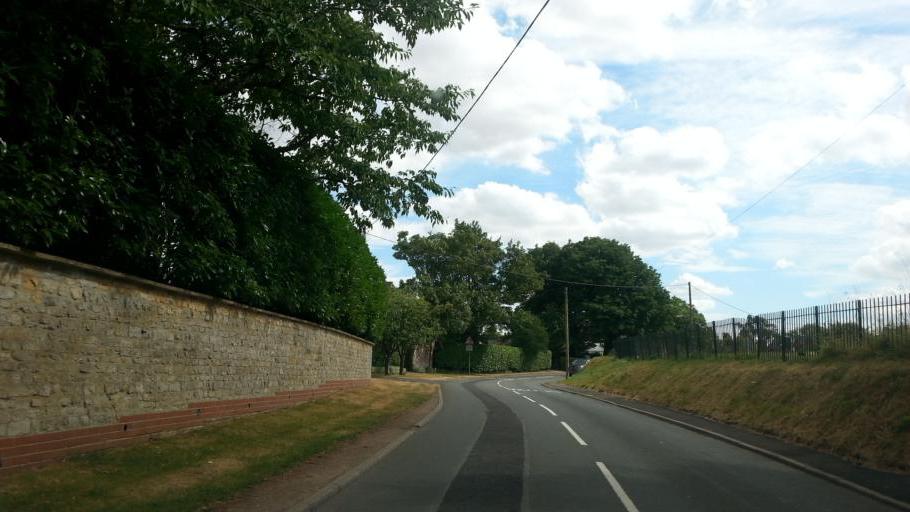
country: GB
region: England
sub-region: Northamptonshire
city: Silverstone
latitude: 52.0923
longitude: -0.9937
